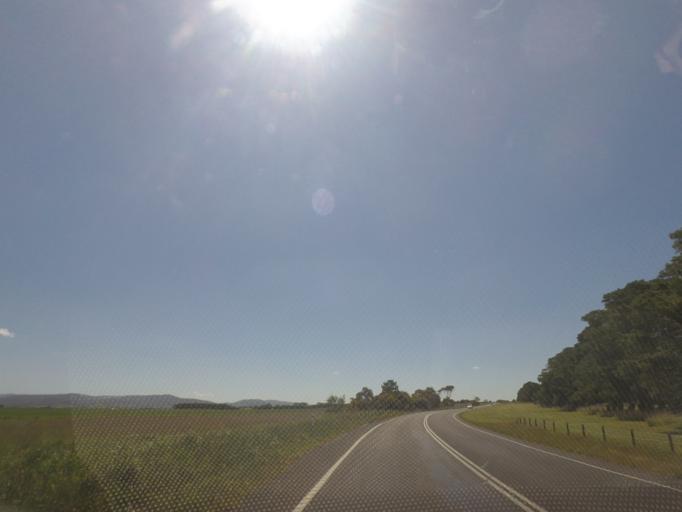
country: AU
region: Victoria
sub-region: Hume
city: Sunbury
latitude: -37.4625
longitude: 144.7415
